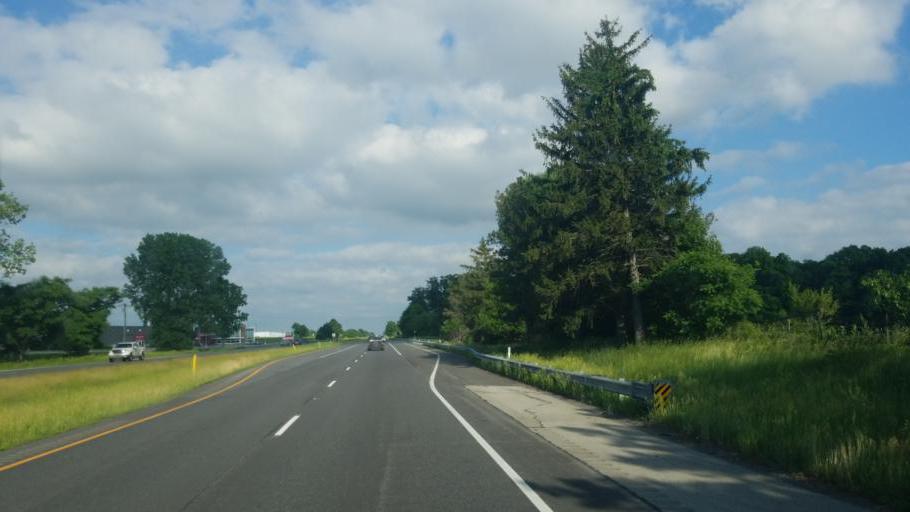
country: US
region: Indiana
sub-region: Whitley County
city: Columbia City
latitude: 41.1366
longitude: -85.4176
